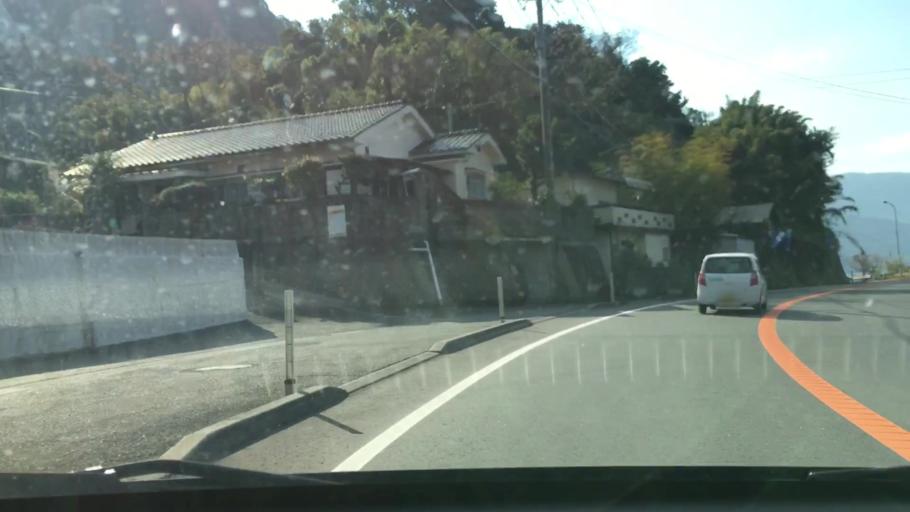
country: JP
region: Kagoshima
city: Hamanoichi
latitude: 31.5990
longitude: 130.7883
